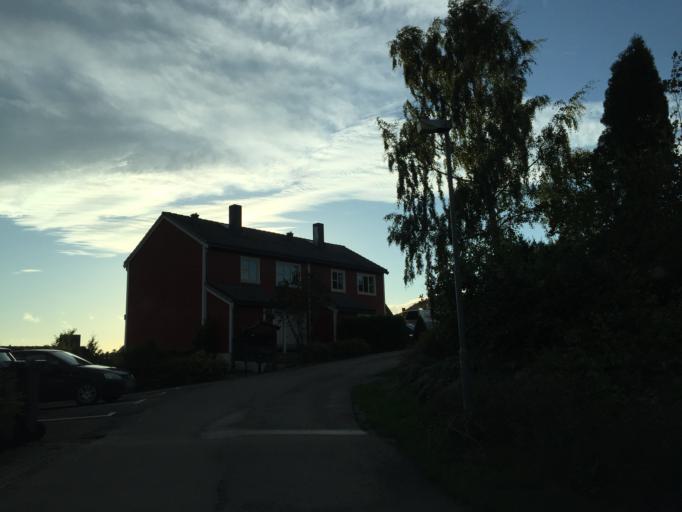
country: NO
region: Akershus
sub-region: Ski
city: Ski
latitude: 59.7617
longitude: 10.8503
